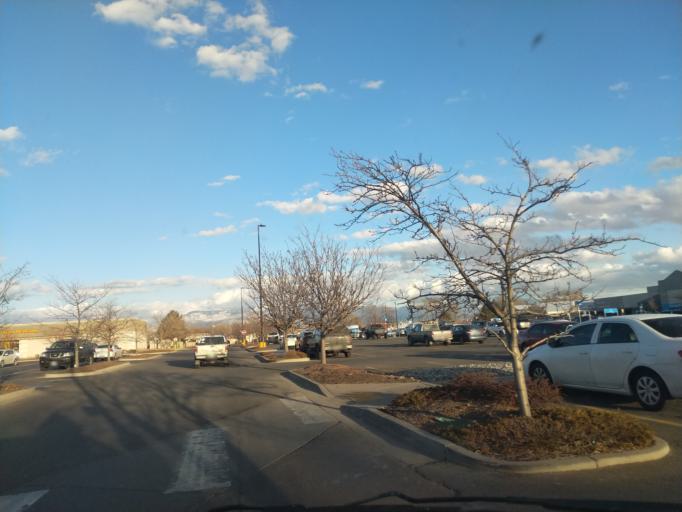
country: US
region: Colorado
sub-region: Mesa County
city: Fruitvale
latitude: 39.0766
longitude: -108.5196
